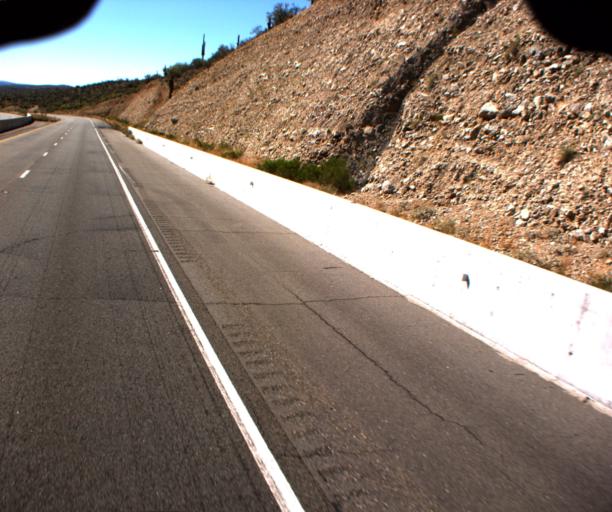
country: US
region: Arizona
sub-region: Yavapai County
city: Bagdad
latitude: 34.4015
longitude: -113.2196
